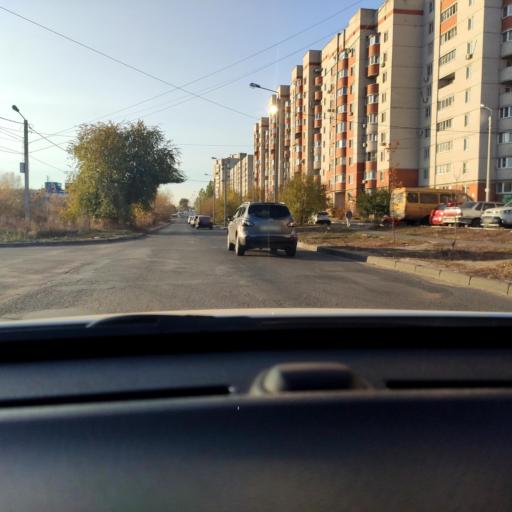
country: RU
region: Voronezj
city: Somovo
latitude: 51.6731
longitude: 39.2910
